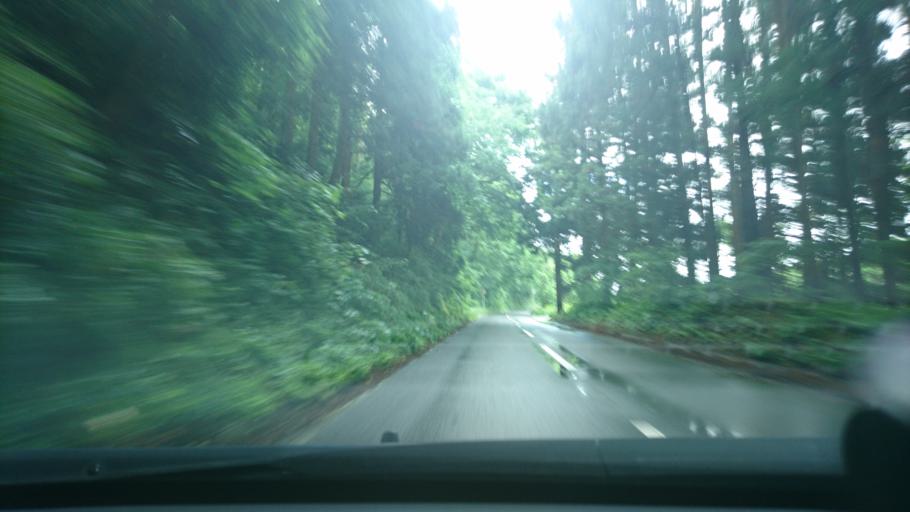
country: JP
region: Miyagi
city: Wakuya
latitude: 38.6715
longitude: 141.2827
